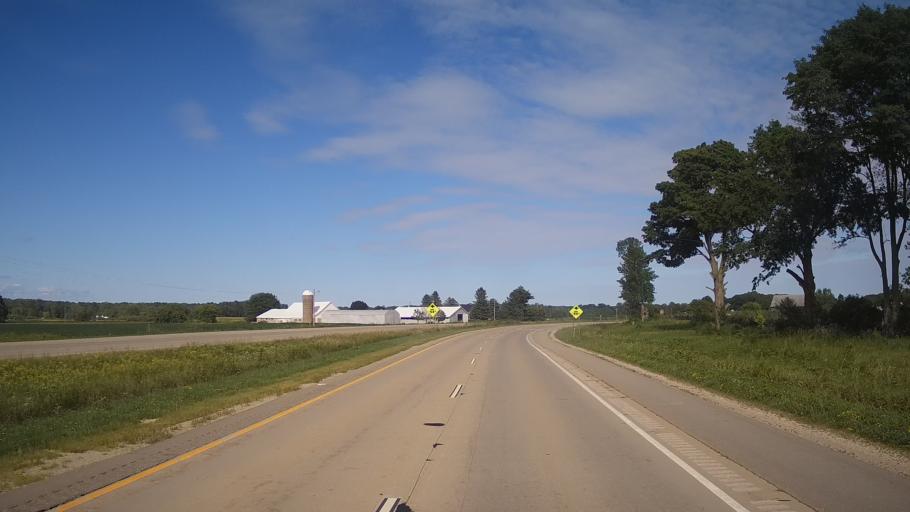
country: US
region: Wisconsin
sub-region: Oconto County
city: Oconto Falls
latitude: 44.7988
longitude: -88.0232
